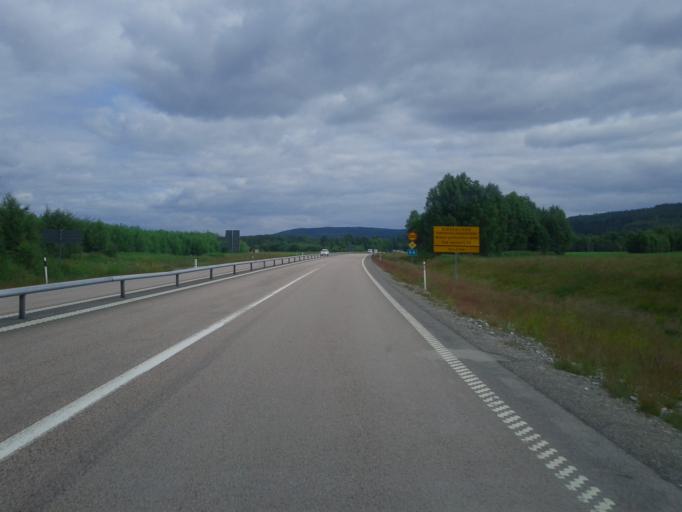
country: SE
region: Vaesternorrland
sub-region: OErnskoeldsviks Kommun
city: Bjasta
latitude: 63.2082
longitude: 18.4883
